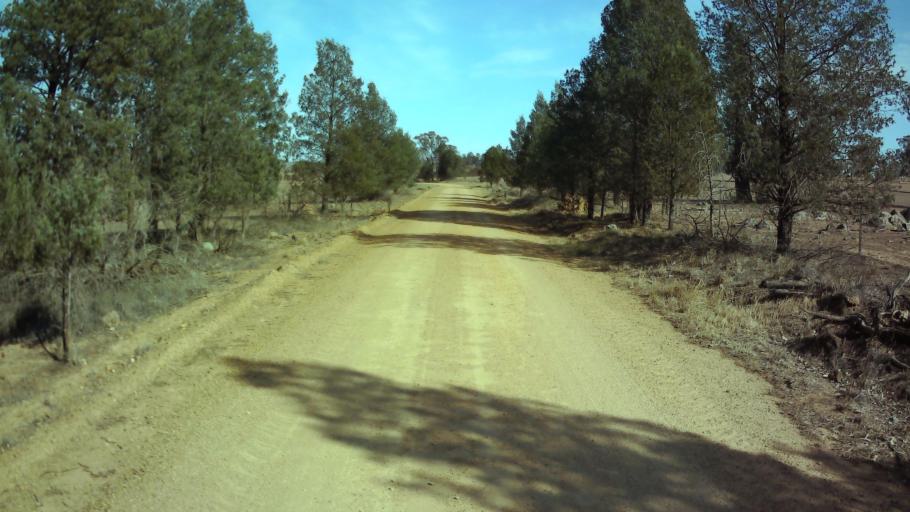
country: AU
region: New South Wales
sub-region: Weddin
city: Grenfell
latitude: -33.7555
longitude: 148.0254
